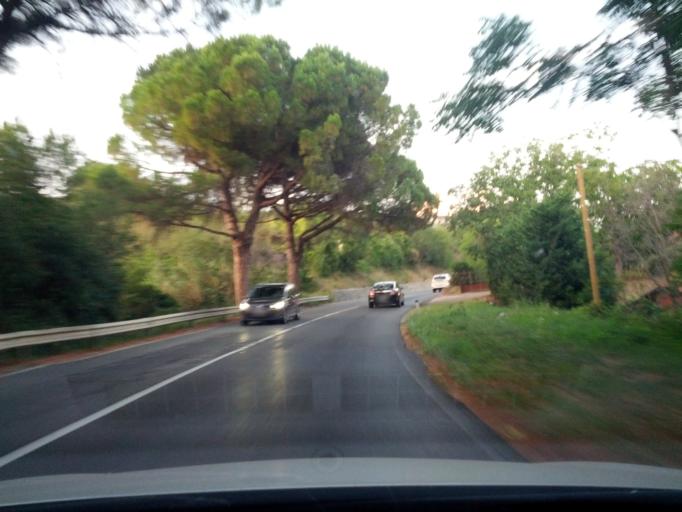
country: SI
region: Izola-Isola
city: Jagodje
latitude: 45.5291
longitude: 13.6247
